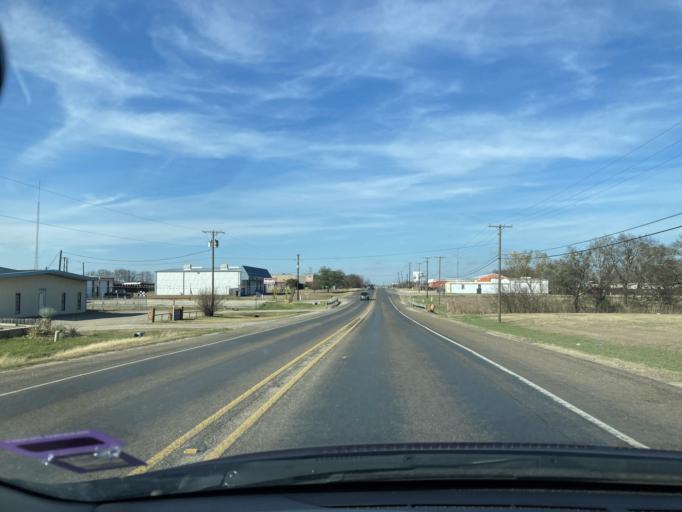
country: US
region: Texas
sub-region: Navarro County
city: Corsicana
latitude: 32.0791
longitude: -96.4488
